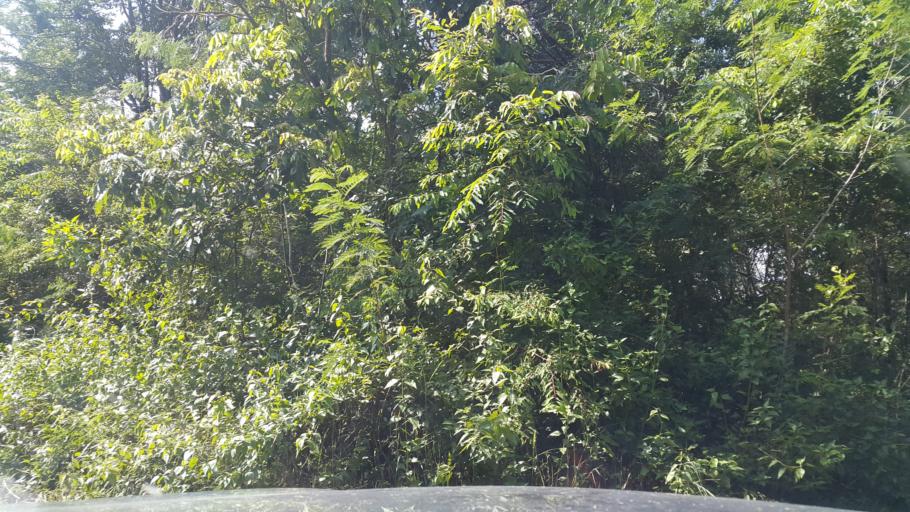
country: TH
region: Chiang Mai
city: San Sai
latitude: 18.9535
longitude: 99.1375
